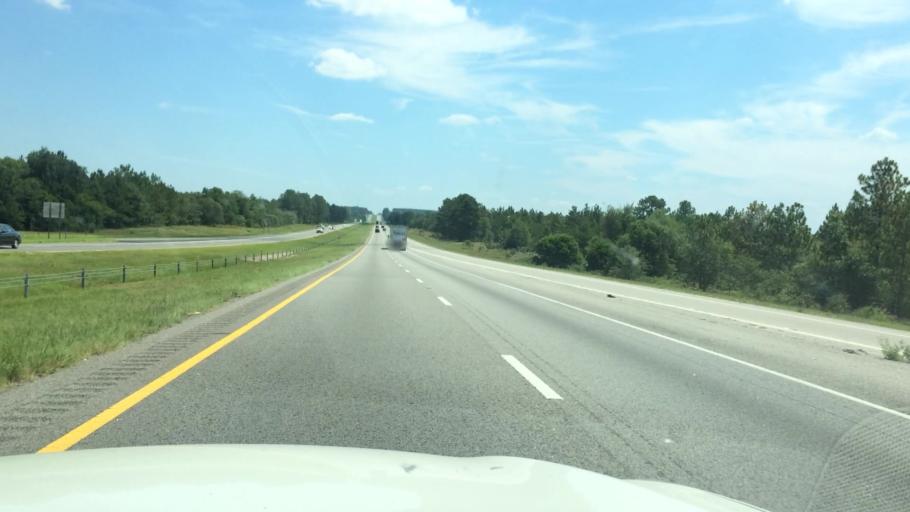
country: US
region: South Carolina
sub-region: Lexington County
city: Batesburg
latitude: 33.7237
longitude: -81.5655
